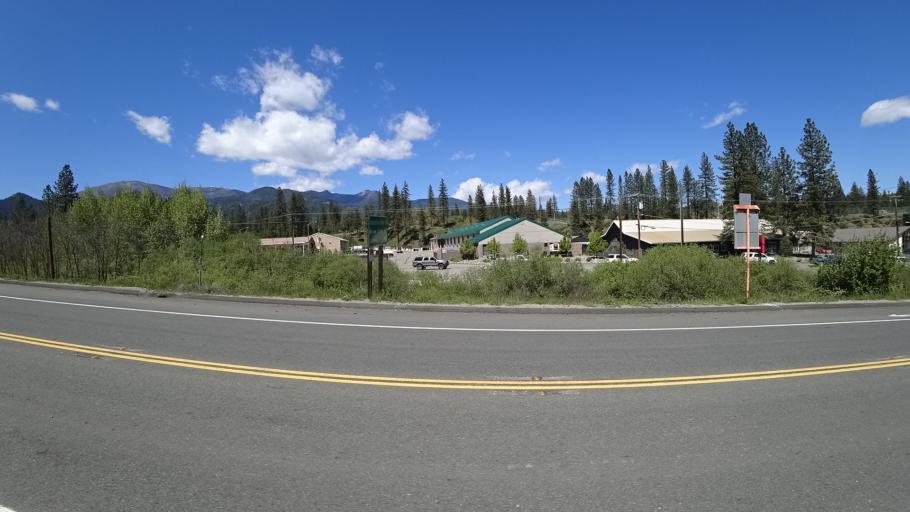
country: US
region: California
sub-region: Trinity County
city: Weaverville
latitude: 40.7362
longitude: -122.9485
